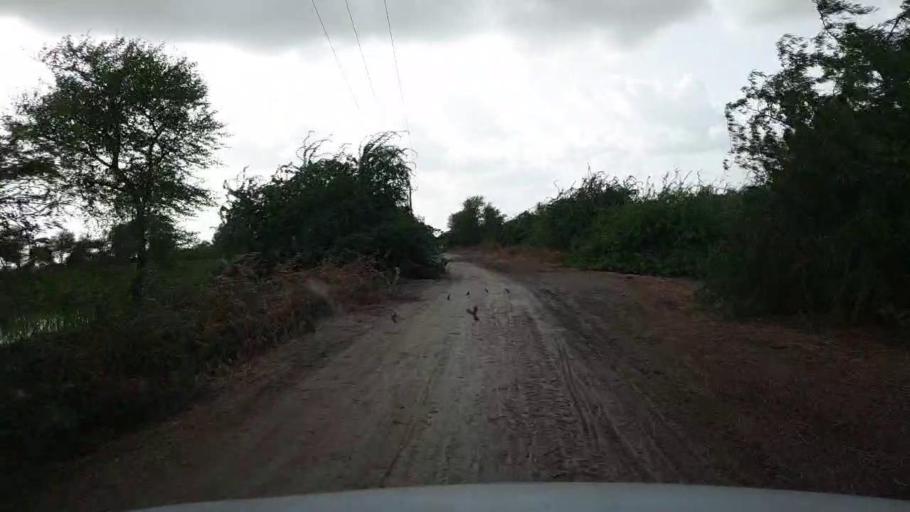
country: PK
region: Sindh
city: Kario
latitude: 24.7543
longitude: 68.6112
